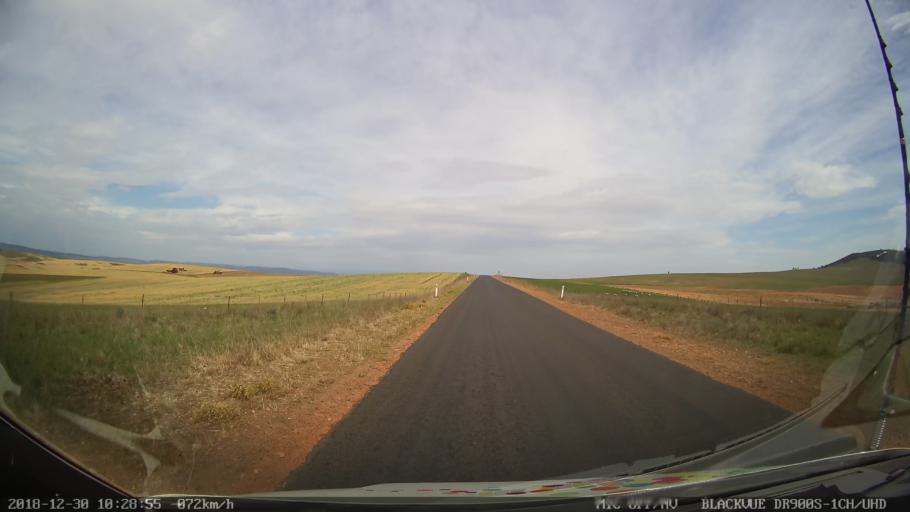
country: AU
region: New South Wales
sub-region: Snowy River
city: Berridale
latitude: -36.5040
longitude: 148.9157
